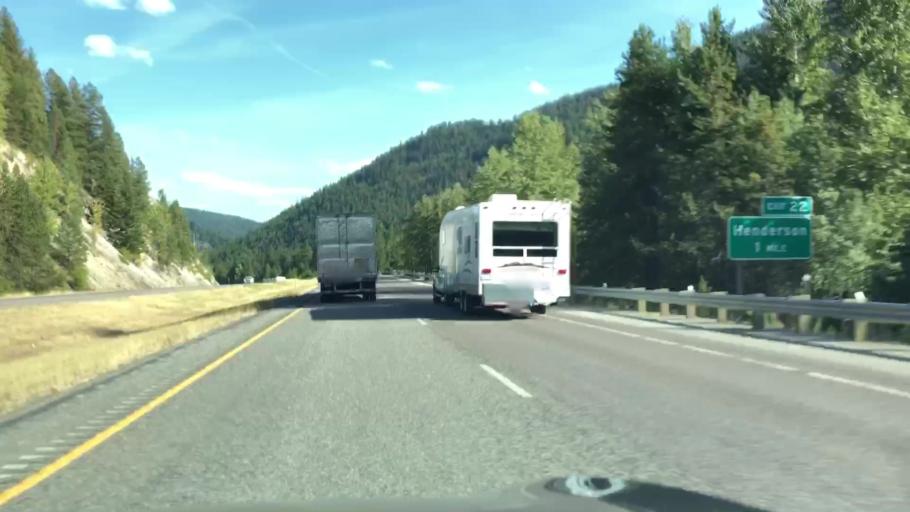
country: US
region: Montana
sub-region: Sanders County
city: Thompson Falls
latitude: 47.3616
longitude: -115.3210
